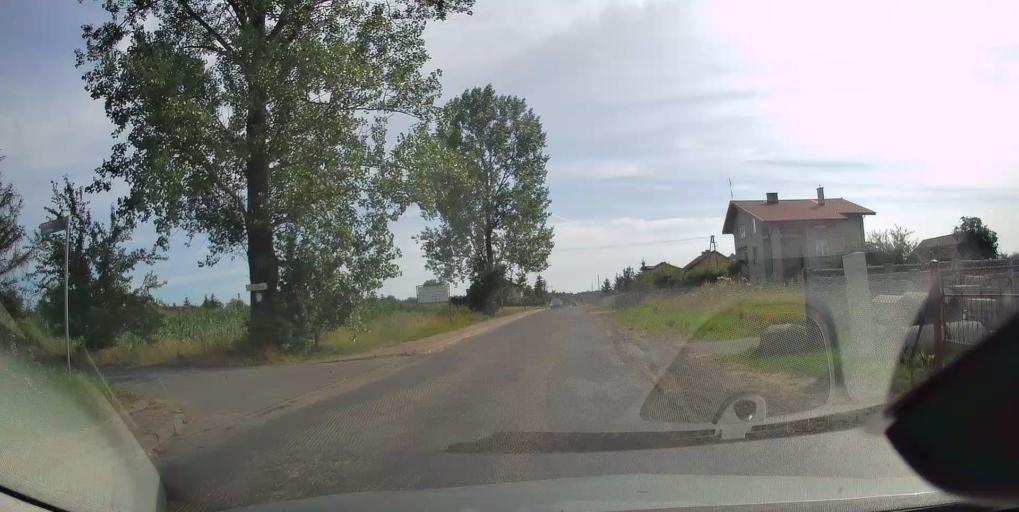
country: PL
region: Lodz Voivodeship
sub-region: Powiat opoczynski
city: Mniszkow
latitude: 51.4525
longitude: 20.0334
